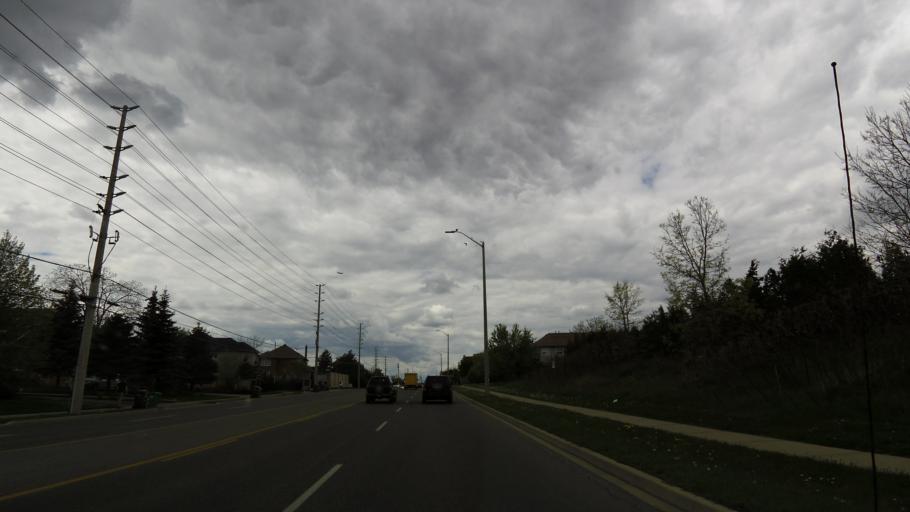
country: CA
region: Ontario
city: Mississauga
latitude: 43.5853
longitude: -79.6951
